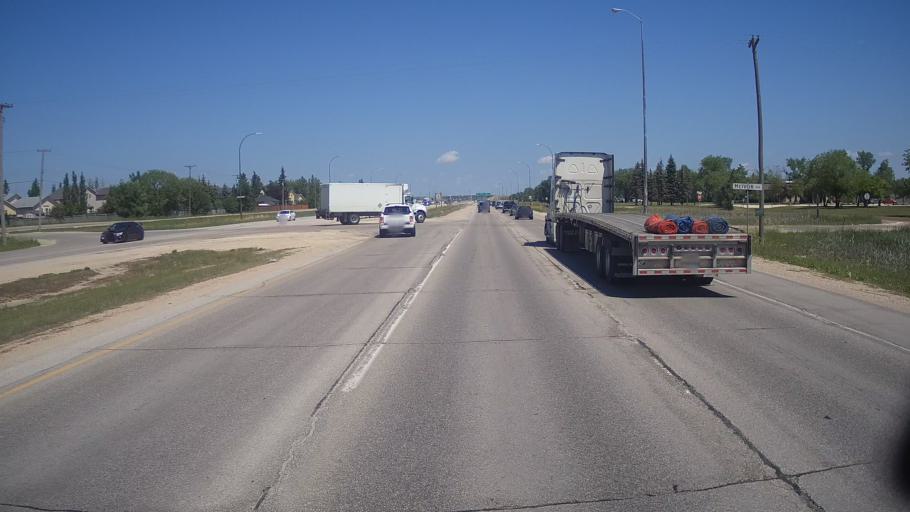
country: CA
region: Manitoba
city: Winnipeg
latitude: 49.9371
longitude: -97.0391
